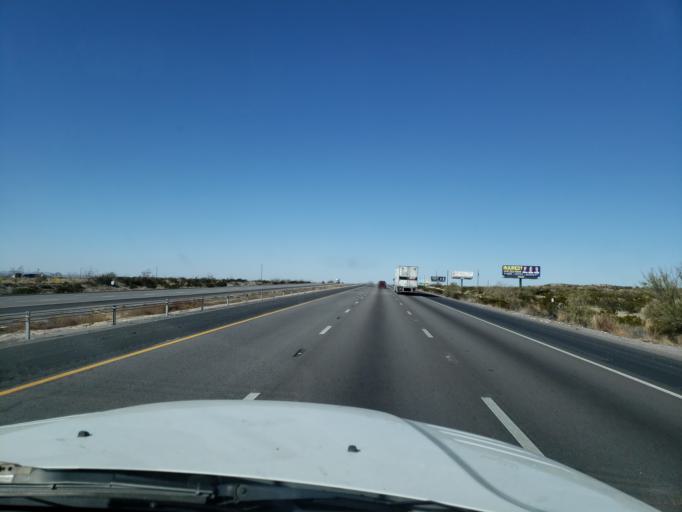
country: US
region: New Mexico
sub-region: Dona Ana County
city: Mesquite
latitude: 32.1845
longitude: -106.6773
